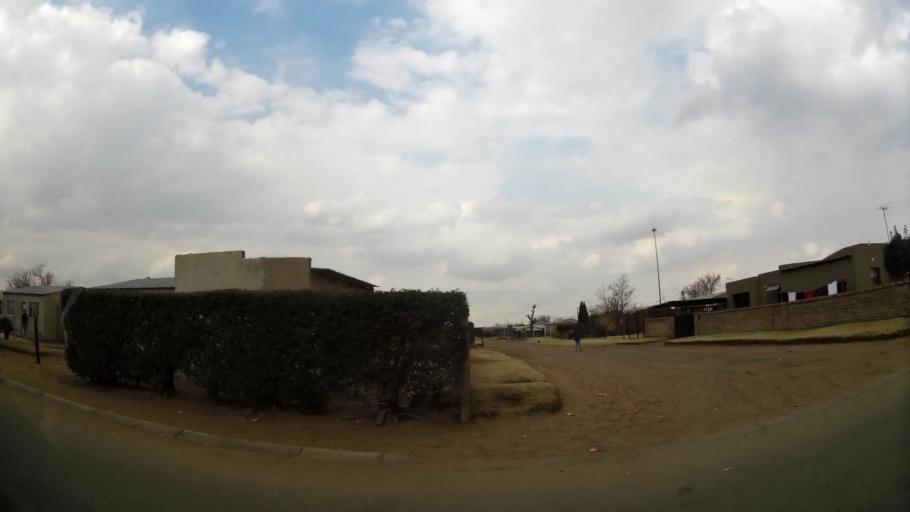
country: ZA
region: Orange Free State
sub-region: Fezile Dabi District Municipality
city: Sasolburg
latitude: -26.8533
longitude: 27.8770
